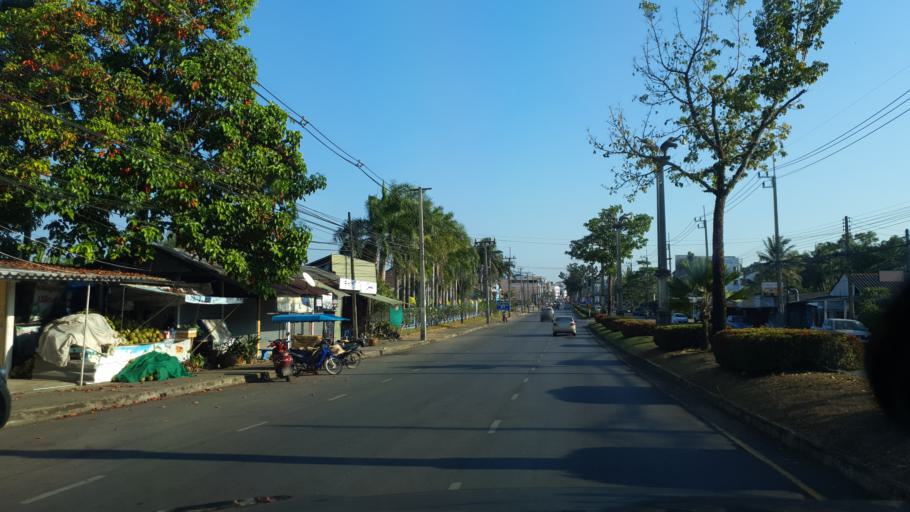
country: TH
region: Krabi
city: Krabi
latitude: 8.0724
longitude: 98.9117
